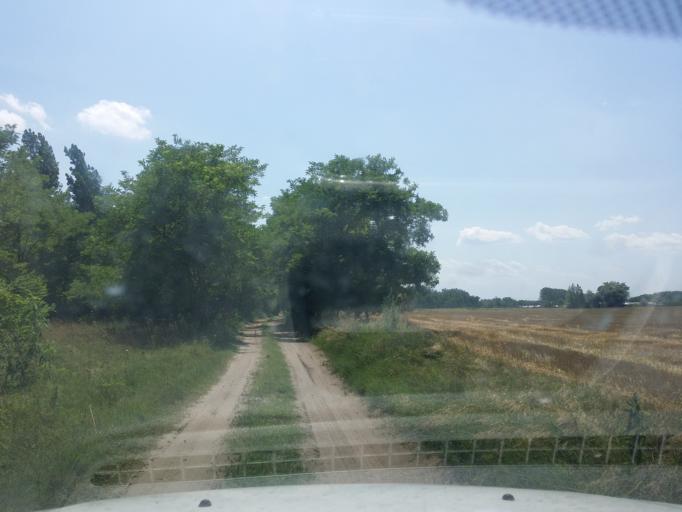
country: HU
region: Bacs-Kiskun
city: Szank
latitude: 46.5993
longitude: 19.7071
